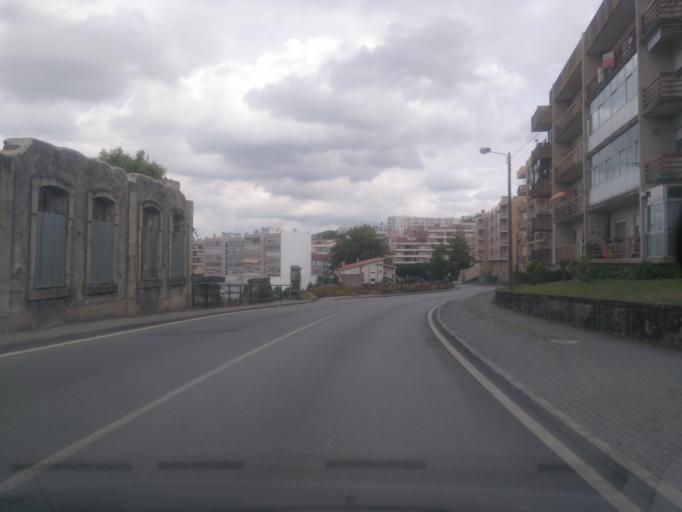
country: PT
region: Braga
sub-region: Braga
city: Braga
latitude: 41.5511
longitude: -8.4380
